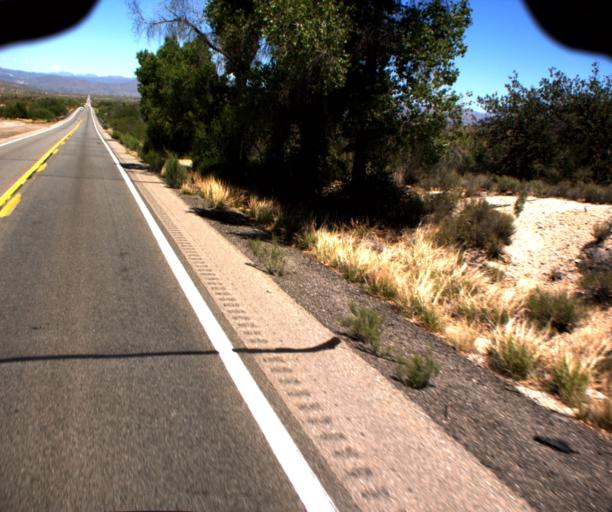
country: US
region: Arizona
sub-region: Yavapai County
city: Bagdad
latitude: 34.3019
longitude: -113.1197
